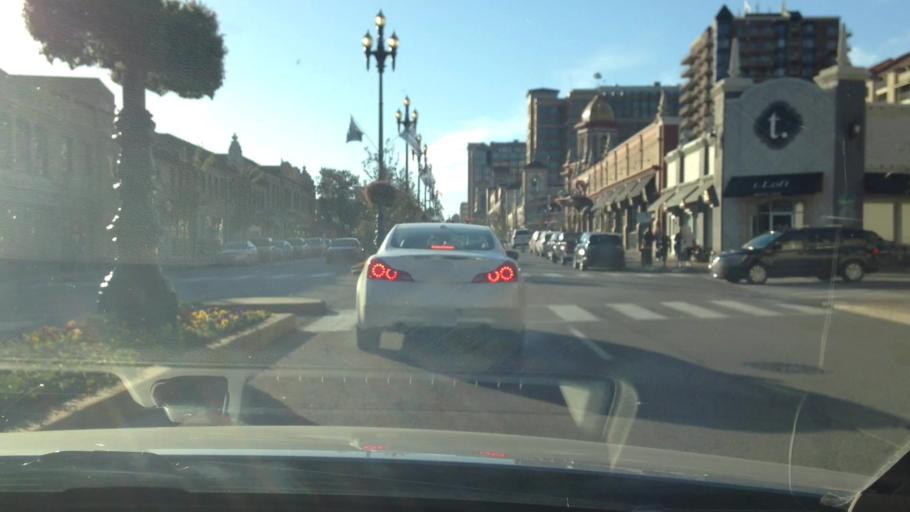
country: US
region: Kansas
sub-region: Johnson County
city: Westwood
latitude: 39.0423
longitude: -94.5890
